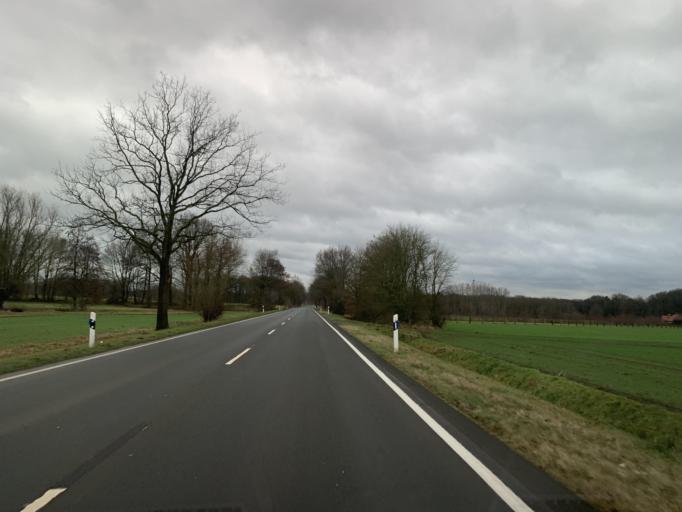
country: DE
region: North Rhine-Westphalia
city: Olfen
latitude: 51.7483
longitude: 7.3291
